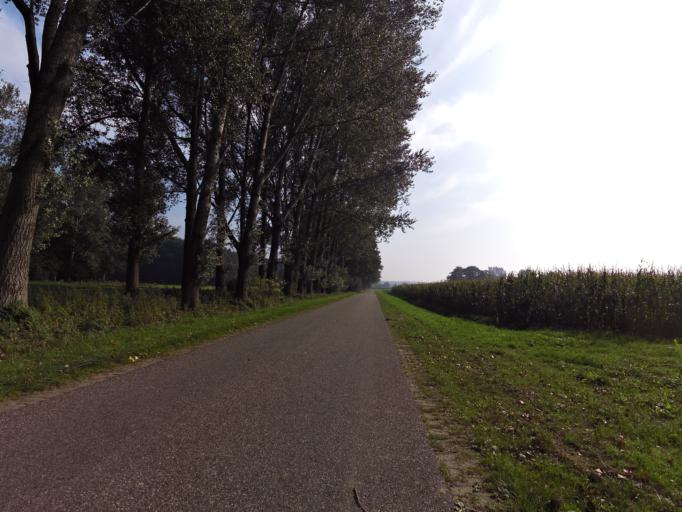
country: NL
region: Gelderland
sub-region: Gemeente Doesburg
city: Doesburg
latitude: 51.9521
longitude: 6.1771
